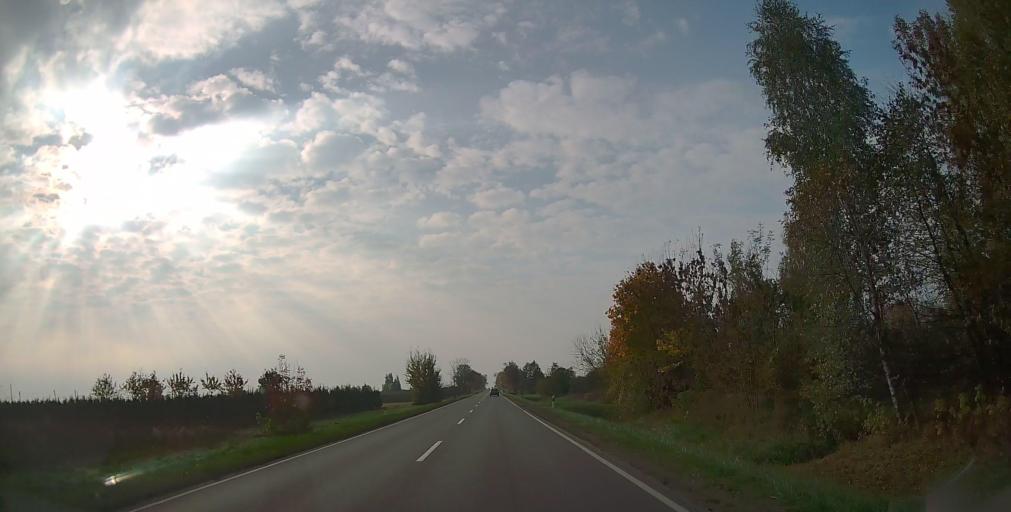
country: PL
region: Masovian Voivodeship
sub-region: Powiat grojecki
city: Bledow
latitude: 51.7590
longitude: 20.7662
